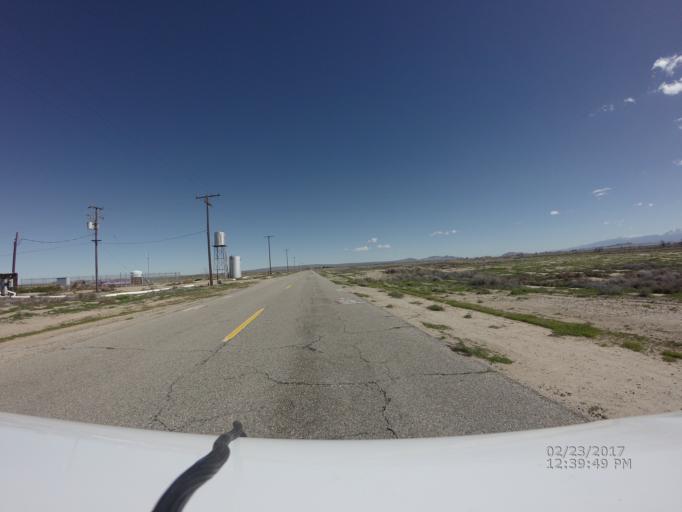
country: US
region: California
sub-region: Los Angeles County
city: Lancaster
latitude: 34.7489
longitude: -117.9886
